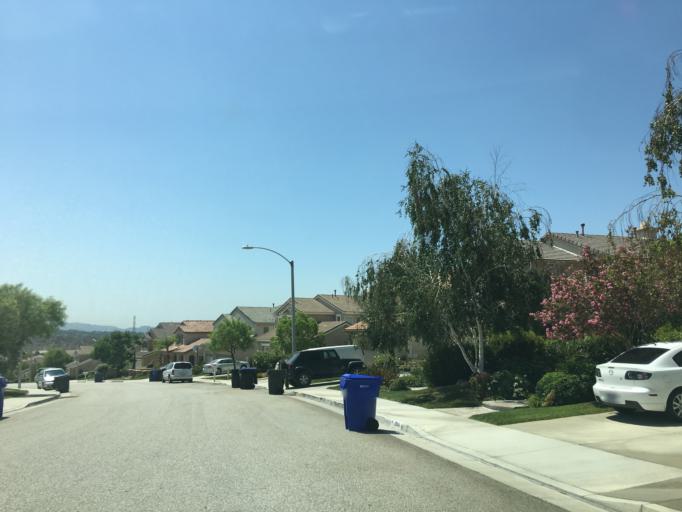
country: US
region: California
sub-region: Los Angeles County
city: Valencia
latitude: 34.4656
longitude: -118.5617
